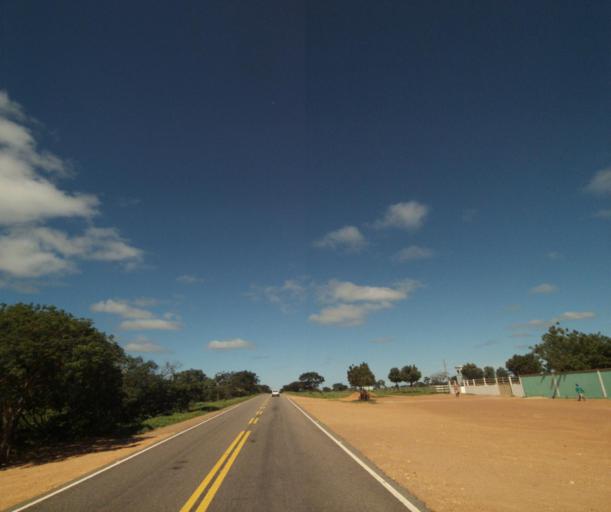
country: BR
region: Bahia
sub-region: Palmas De Monte Alto
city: Palmas de Monte Alto
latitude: -14.2403
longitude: -43.0480
